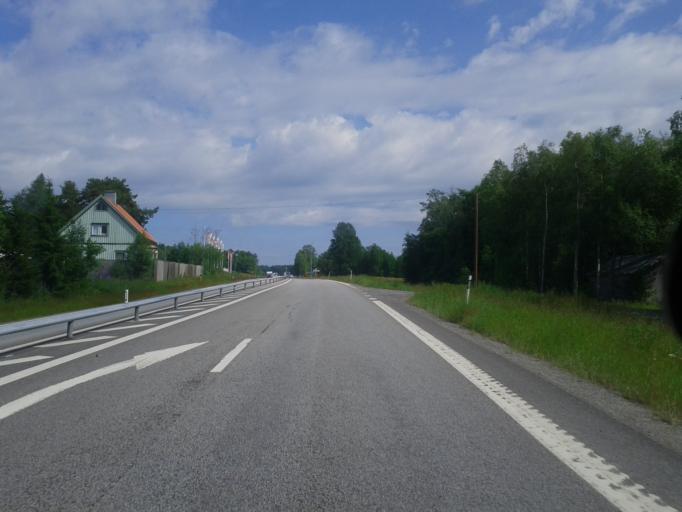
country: SE
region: Vaesternorrland
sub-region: OErnskoeldsviks Kommun
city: Ornskoldsvik
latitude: 63.2987
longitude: 18.8974
